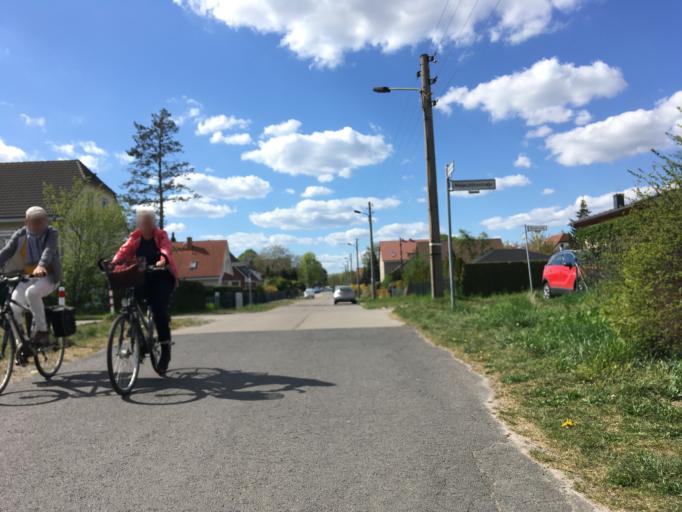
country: DE
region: Berlin
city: Mahlsdorf
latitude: 52.5184
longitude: 13.6190
